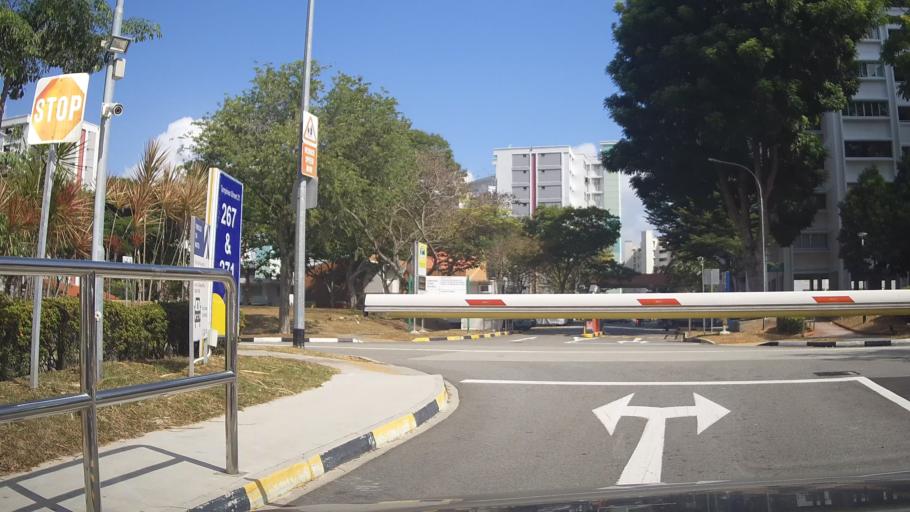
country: SG
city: Singapore
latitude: 1.3512
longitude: 103.9494
